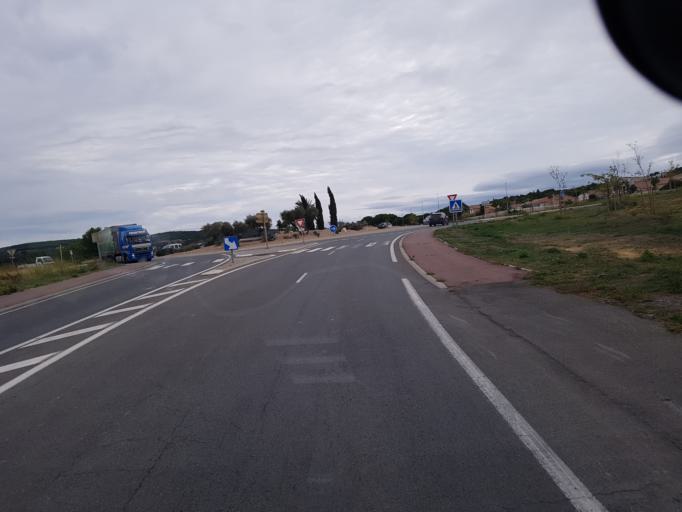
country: FR
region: Languedoc-Roussillon
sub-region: Departement de l'Aude
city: Narbonne
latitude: 43.1456
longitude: 2.9760
